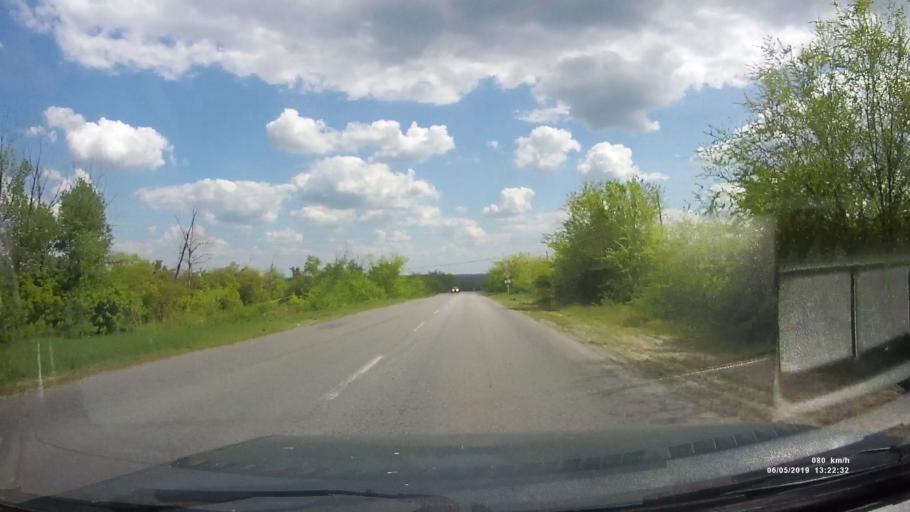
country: RU
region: Rostov
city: Ust'-Donetskiy
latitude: 47.6953
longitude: 40.9214
